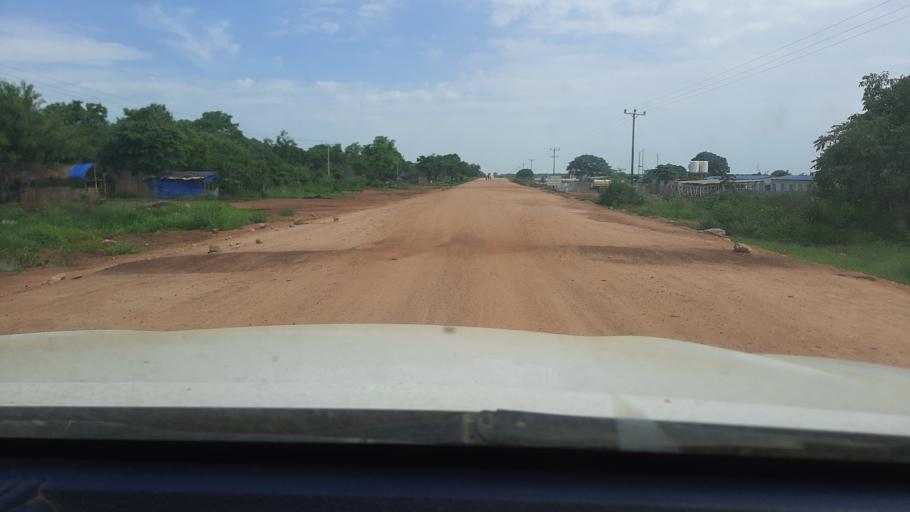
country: ET
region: Gambela
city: Gambela
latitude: 8.0337
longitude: 34.5772
